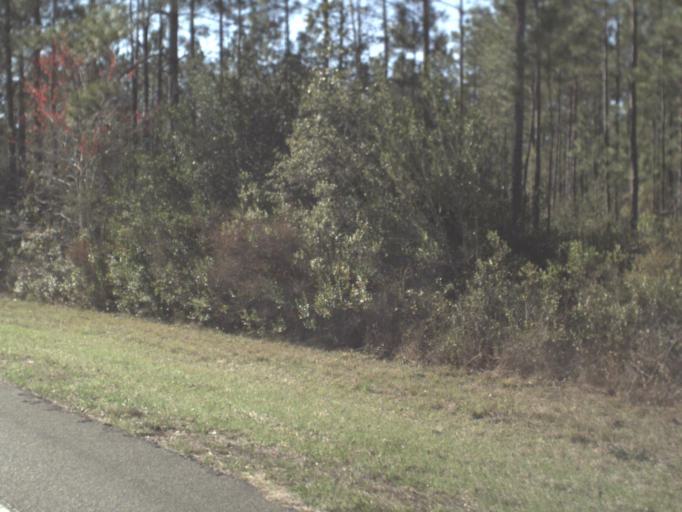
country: US
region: Florida
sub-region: Calhoun County
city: Blountstown
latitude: 30.4307
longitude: -85.1025
